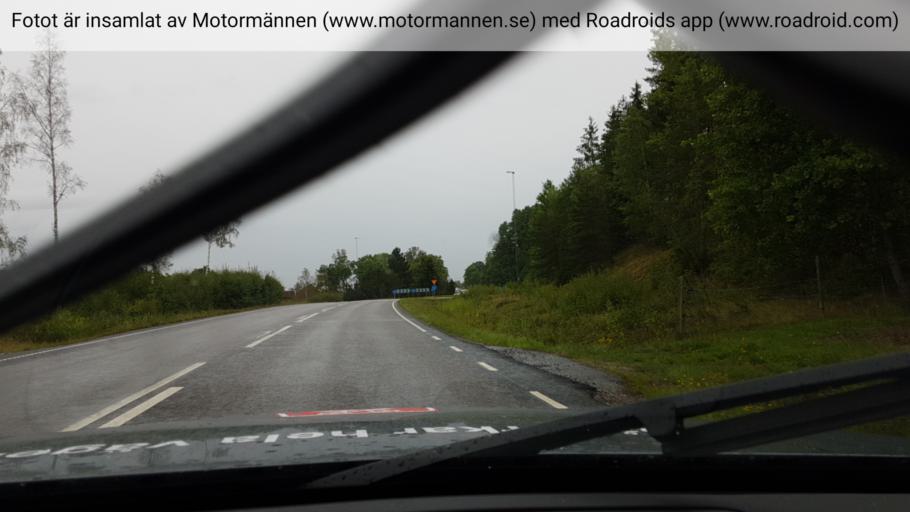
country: SE
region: Soedermanland
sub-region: Eskilstuna Kommun
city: Skogstorp
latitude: 59.3191
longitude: 16.5321
